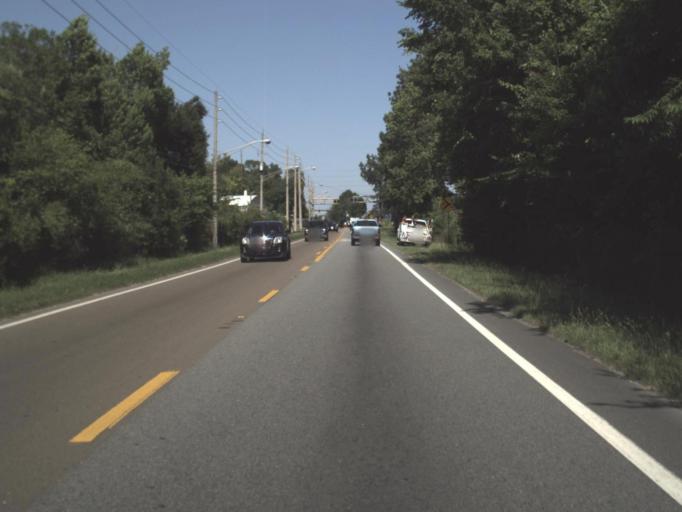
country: US
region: Florida
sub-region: Duval County
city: Jacksonville
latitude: 30.3248
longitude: -81.7475
